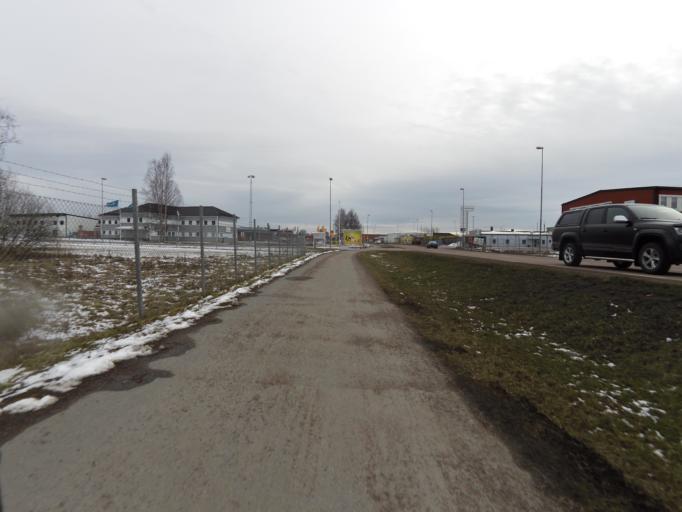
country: SE
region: Gaevleborg
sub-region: Gavle Kommun
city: Gavle
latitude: 60.6887
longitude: 17.1539
